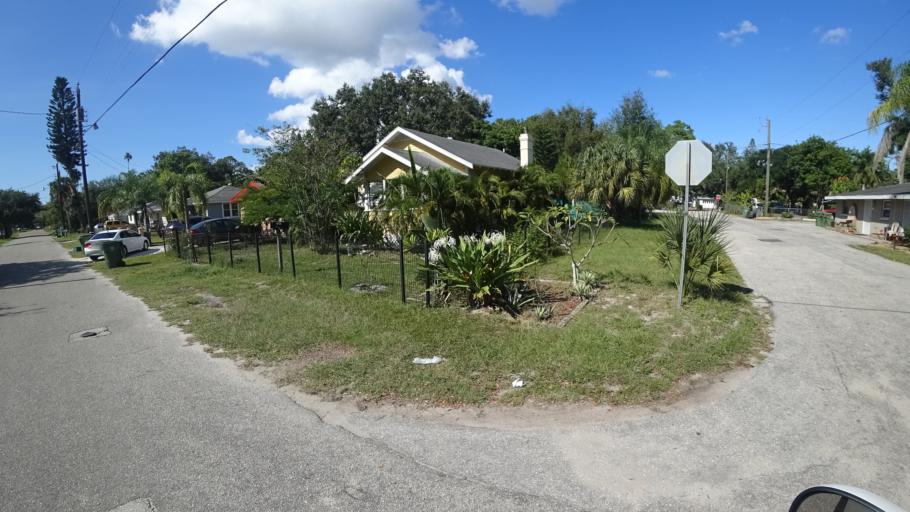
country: US
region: Florida
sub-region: Manatee County
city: Bradenton
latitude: 27.4825
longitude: -82.5767
